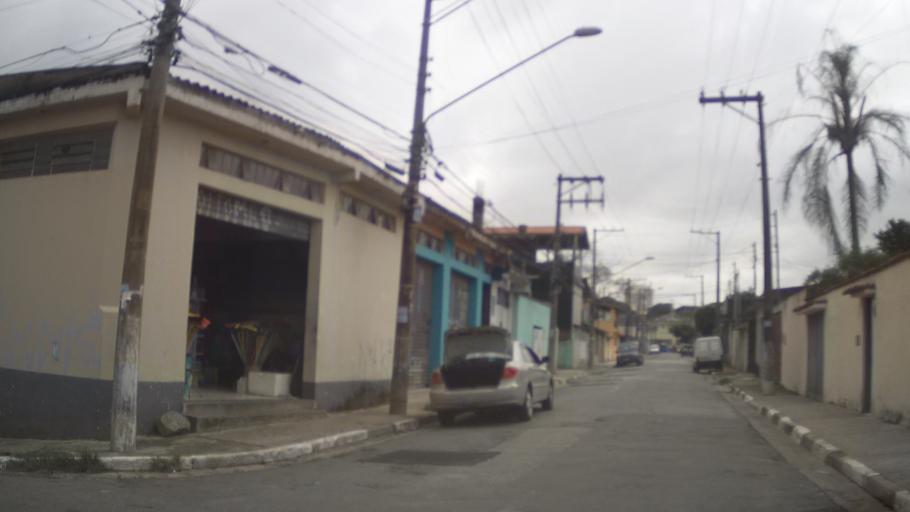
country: BR
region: Sao Paulo
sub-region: Guarulhos
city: Guarulhos
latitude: -23.4733
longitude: -46.5552
